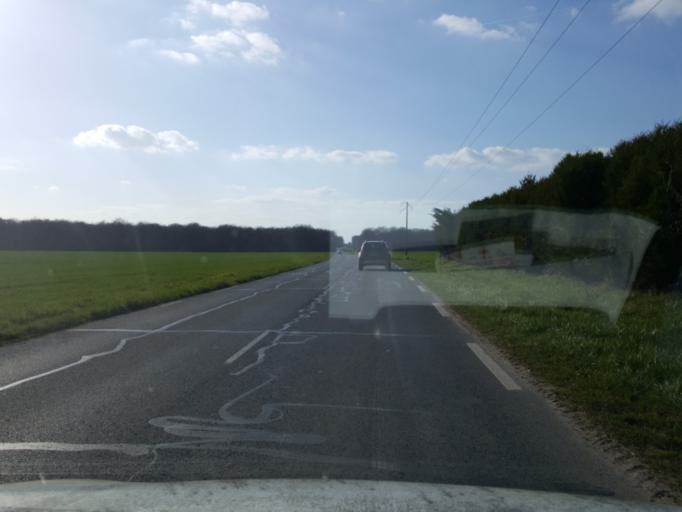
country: FR
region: Ile-de-France
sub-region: Departement des Yvelines
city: Gazeran
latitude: 48.6436
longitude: 1.7439
